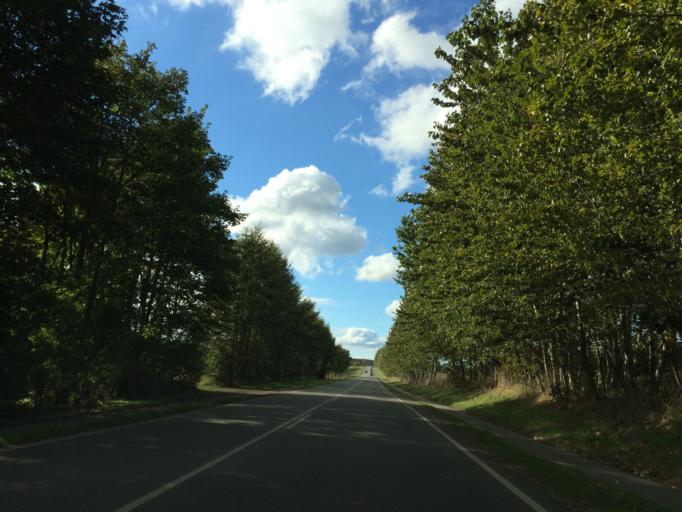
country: DK
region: Central Jutland
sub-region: Skanderborg Kommune
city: Ry
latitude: 56.0821
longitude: 9.7282
